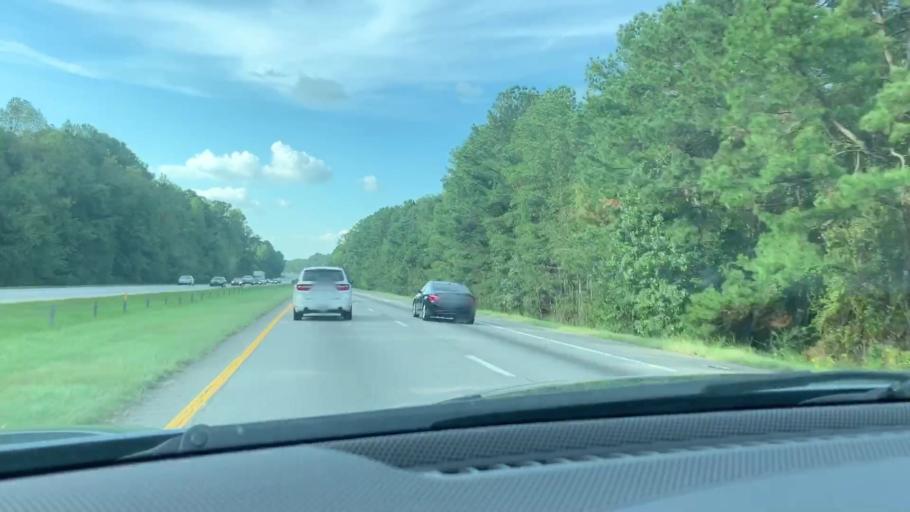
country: US
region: South Carolina
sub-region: Orangeburg County
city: Brookdale
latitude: 33.4902
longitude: -80.7625
